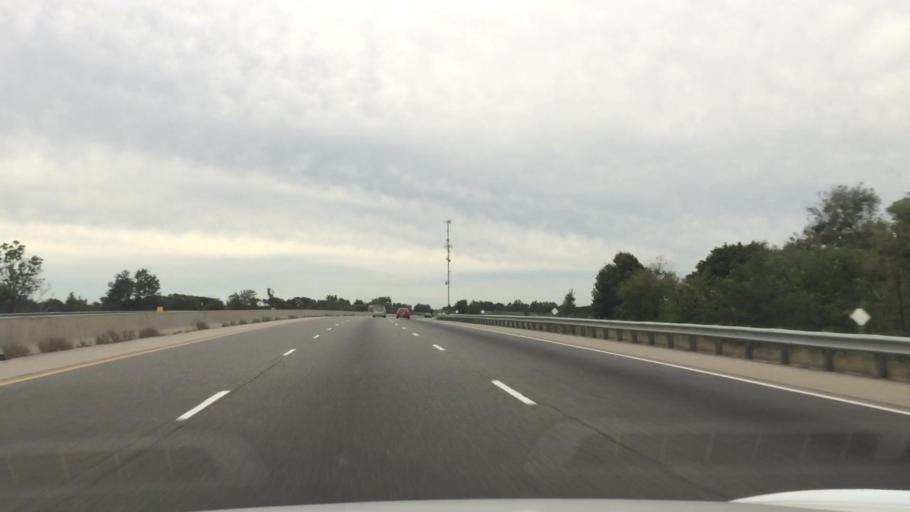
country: CA
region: Ontario
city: Kitchener
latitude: 43.2452
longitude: -80.5725
